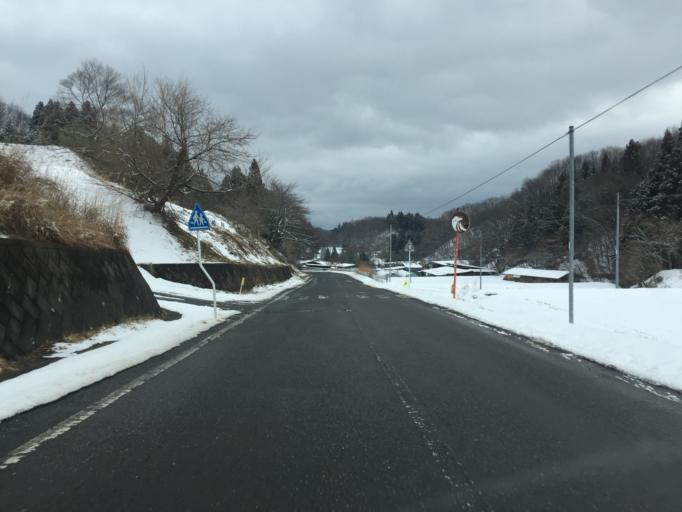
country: JP
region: Fukushima
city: Ishikawa
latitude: 37.1978
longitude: 140.5344
